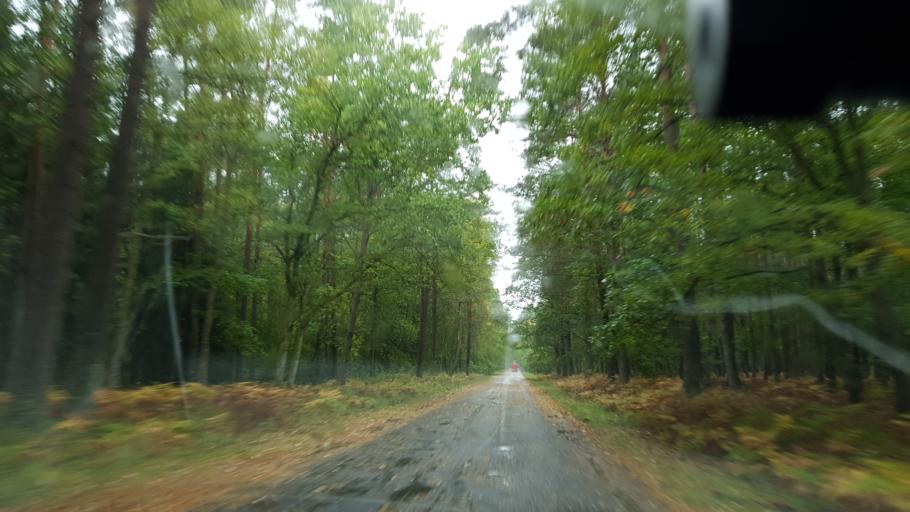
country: PL
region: West Pomeranian Voivodeship
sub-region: Powiat goleniowski
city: Przybiernow
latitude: 53.7085
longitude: 14.7466
